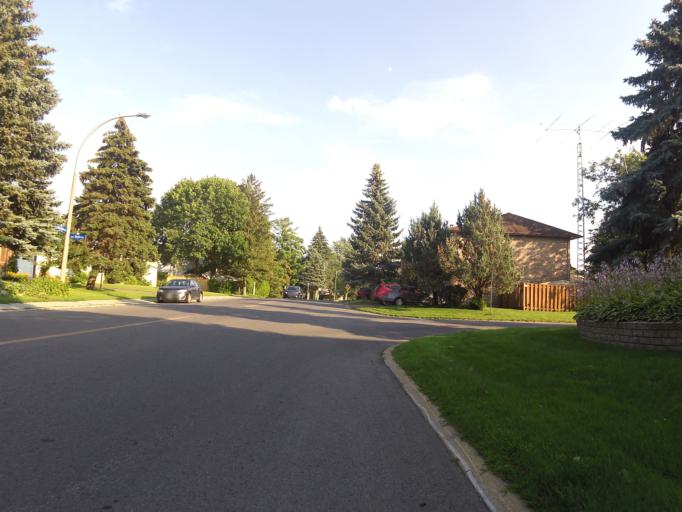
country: CA
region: Ontario
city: Bells Corners
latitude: 45.3299
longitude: -75.7932
